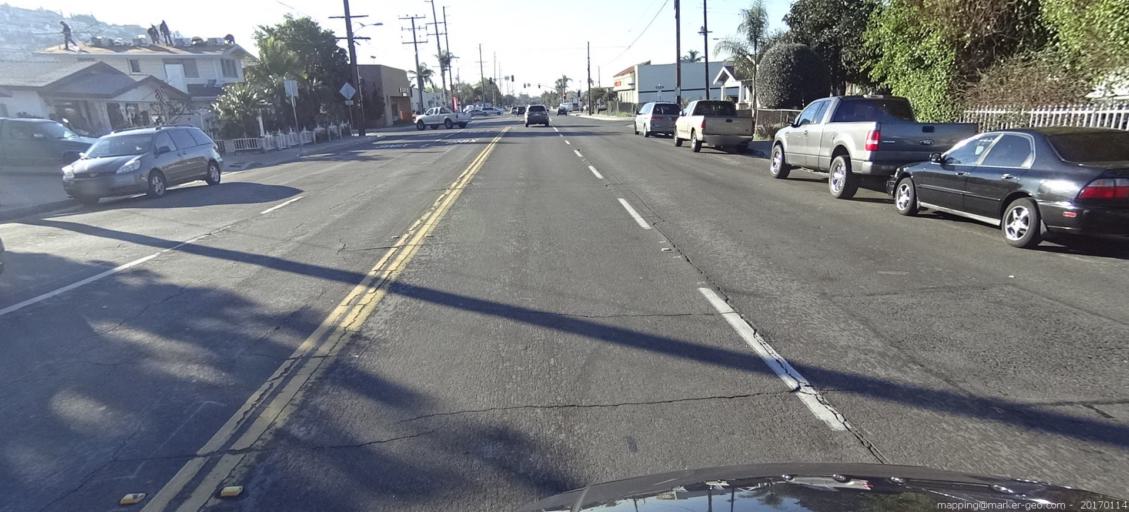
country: US
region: California
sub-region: Orange County
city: Villa Park
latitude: 33.7893
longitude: -117.8057
